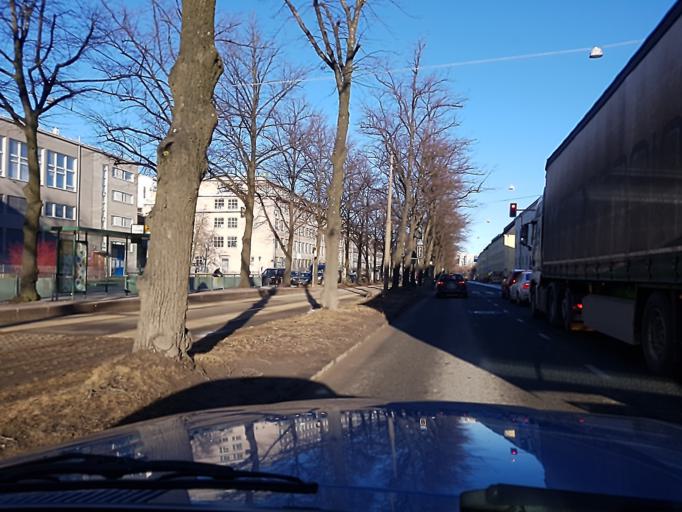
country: FI
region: Uusimaa
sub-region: Helsinki
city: Helsinki
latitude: 60.1959
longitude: 24.9537
